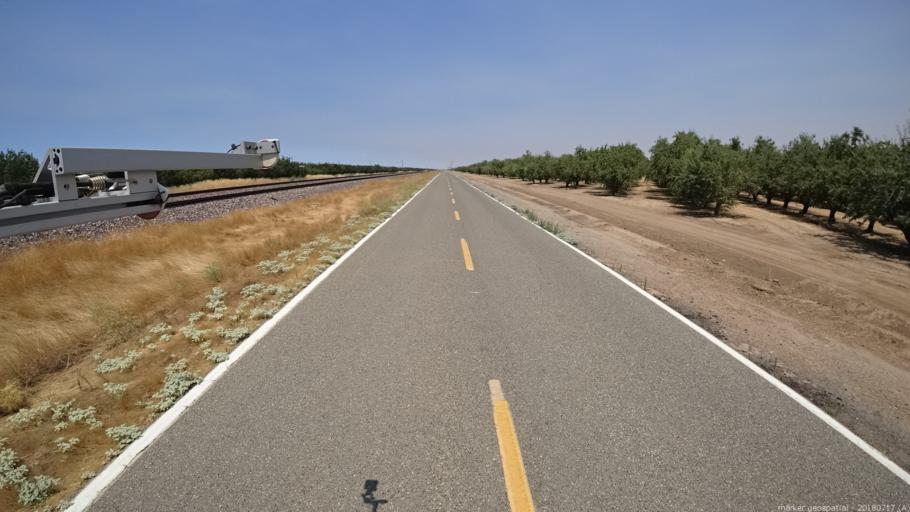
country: US
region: California
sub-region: Madera County
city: Fairmead
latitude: 37.1103
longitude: -120.1390
